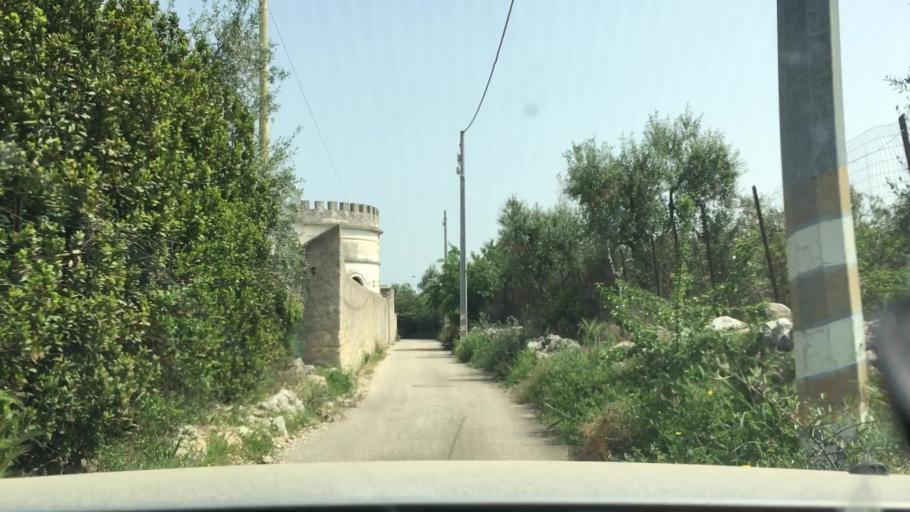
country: IT
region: Apulia
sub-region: Provincia di Barletta - Andria - Trani
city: Capirro
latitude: 41.2543
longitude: 16.4597
